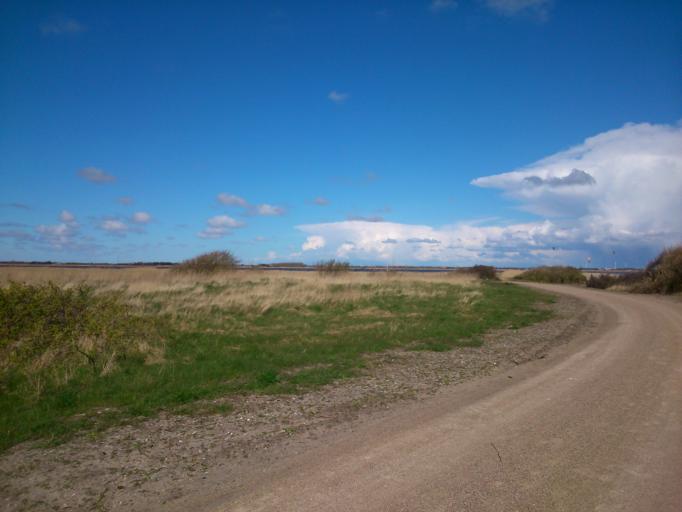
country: DK
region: Central Jutland
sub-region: Ringkobing-Skjern Kommune
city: Hvide Sande
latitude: 56.0988
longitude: 8.1414
